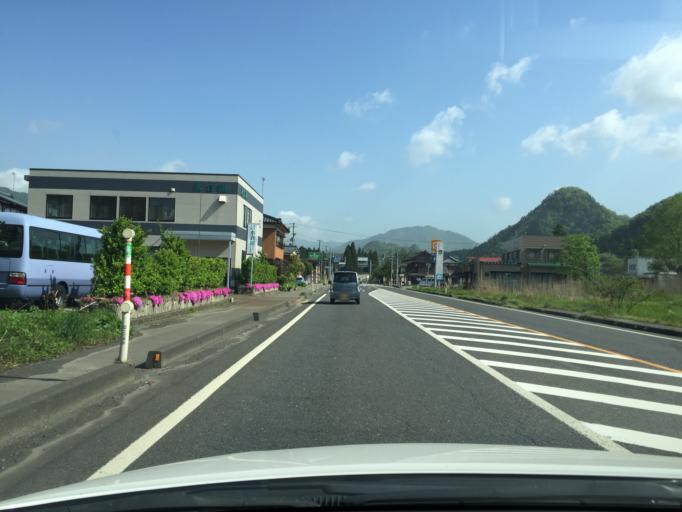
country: JP
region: Niigata
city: Suibara
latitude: 37.7070
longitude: 139.3807
